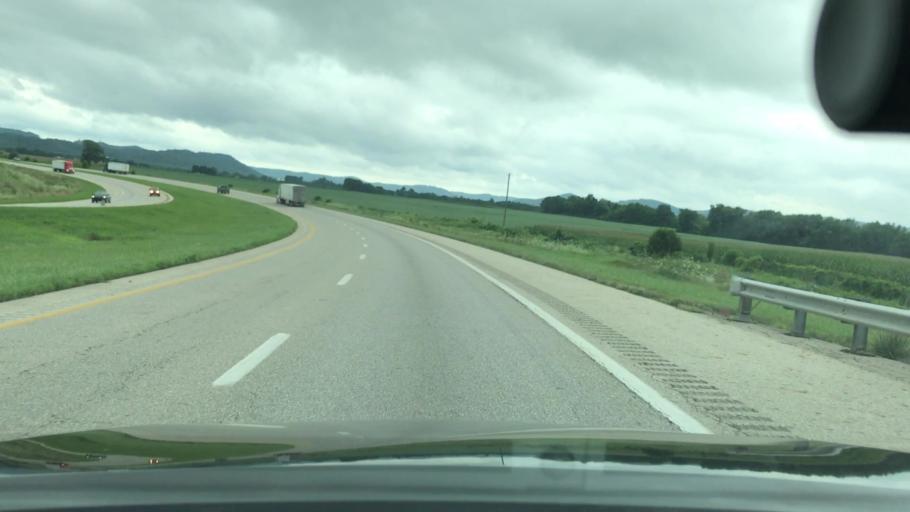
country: US
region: Ohio
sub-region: Ross County
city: Chillicothe
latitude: 39.2727
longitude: -82.8842
